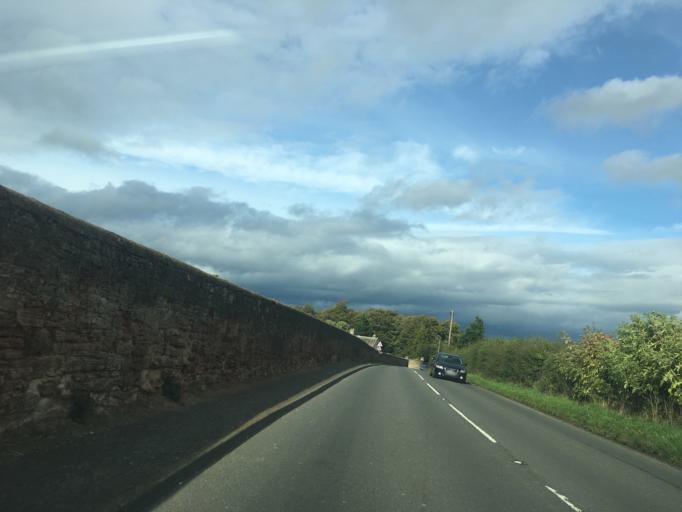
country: GB
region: Scotland
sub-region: East Lothian
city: Musselburgh
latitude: 55.9129
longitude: -3.0446
